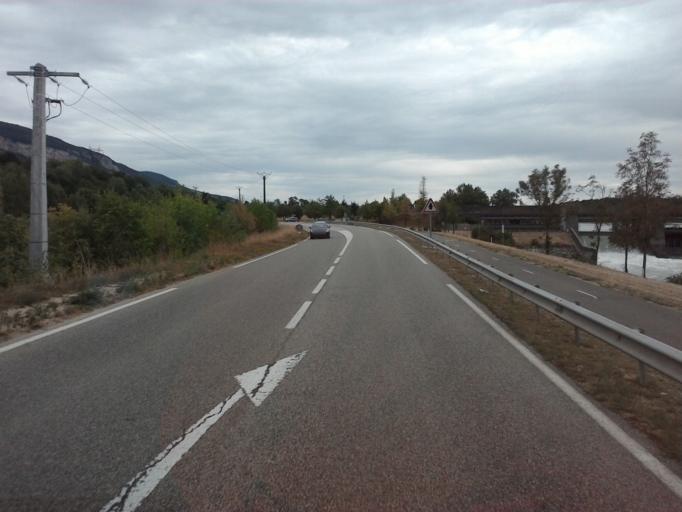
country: FR
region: Rhone-Alpes
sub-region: Departement de l'Ain
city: Sault-Brenaz
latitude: 45.8474
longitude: 5.4181
